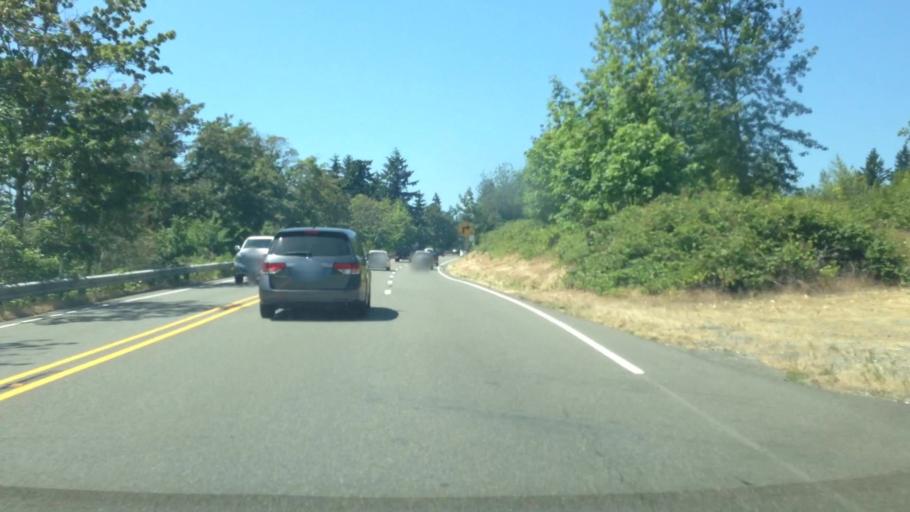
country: US
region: Washington
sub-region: Pierce County
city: North Puyallup
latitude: 47.2158
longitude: -122.2954
